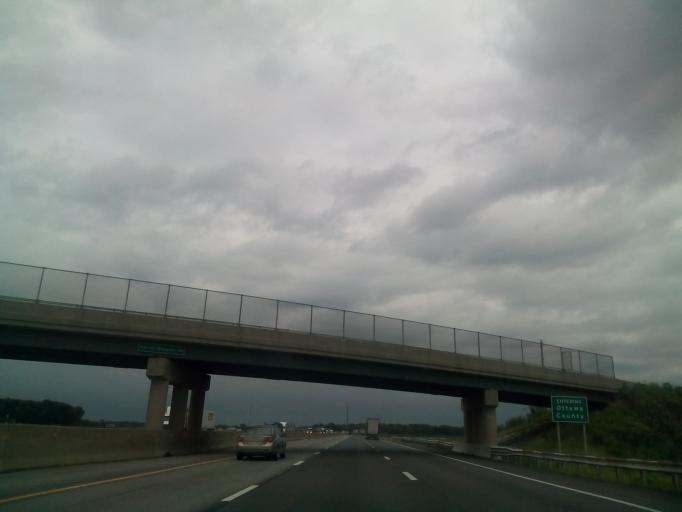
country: US
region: Ohio
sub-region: Sandusky County
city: Woodville
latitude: 41.4767
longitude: -83.3389
